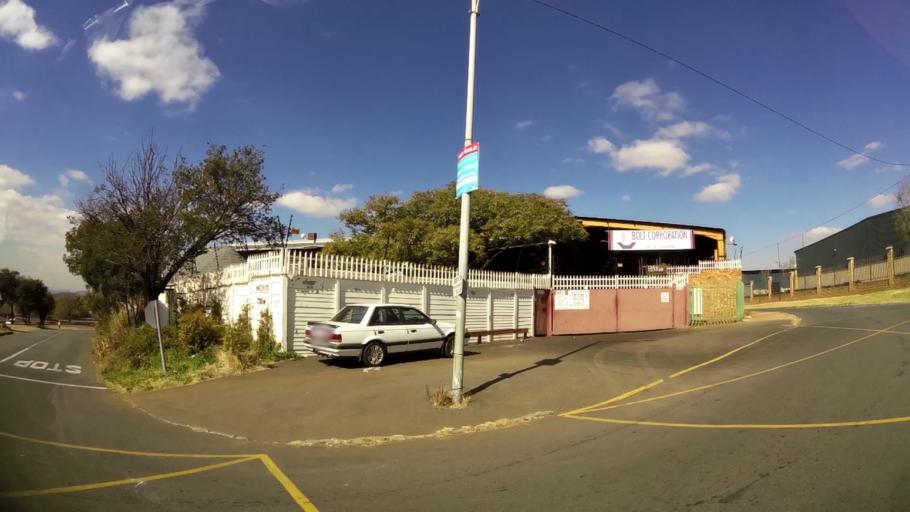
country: ZA
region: Gauteng
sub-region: West Rand District Municipality
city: Krugersdorp
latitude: -26.1140
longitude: 27.8142
